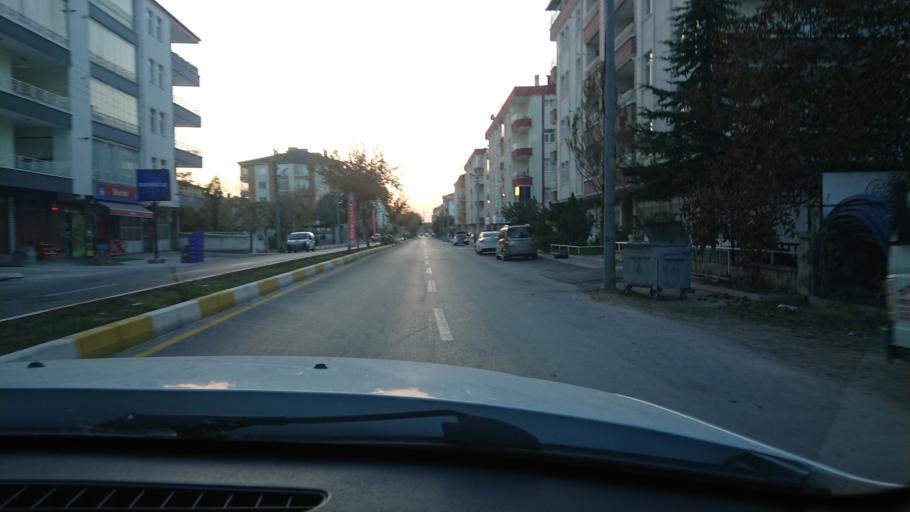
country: TR
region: Aksaray
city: Aksaray
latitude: 38.3634
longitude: 34.0339
